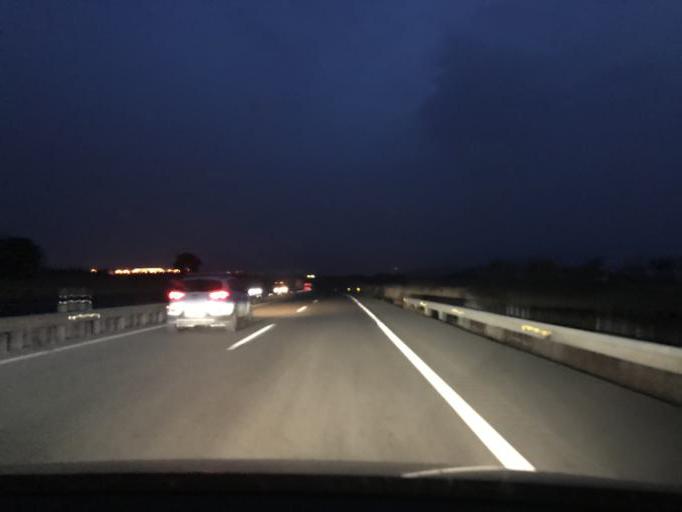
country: ES
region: Andalusia
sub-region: Provincia de Granada
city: Guadix
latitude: 37.3524
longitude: -3.0873
